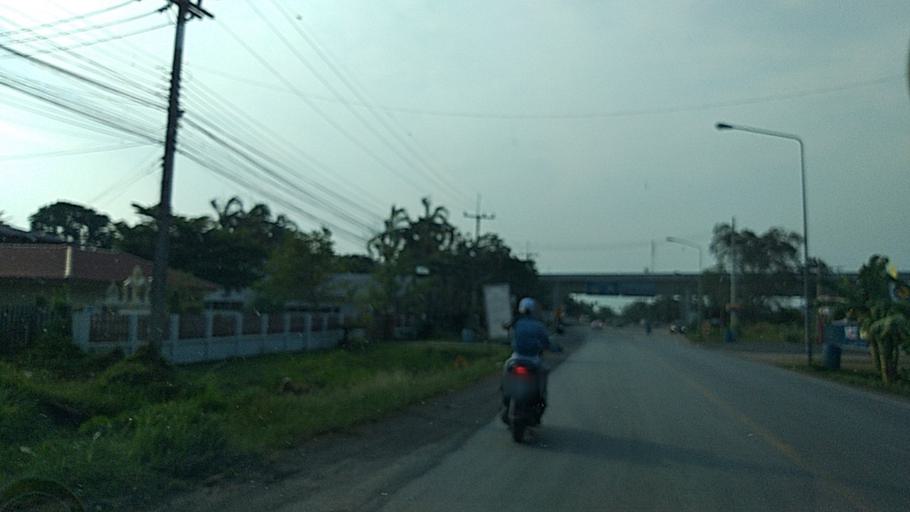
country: TH
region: Sara Buri
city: Saraburi
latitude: 14.4640
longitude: 100.9412
